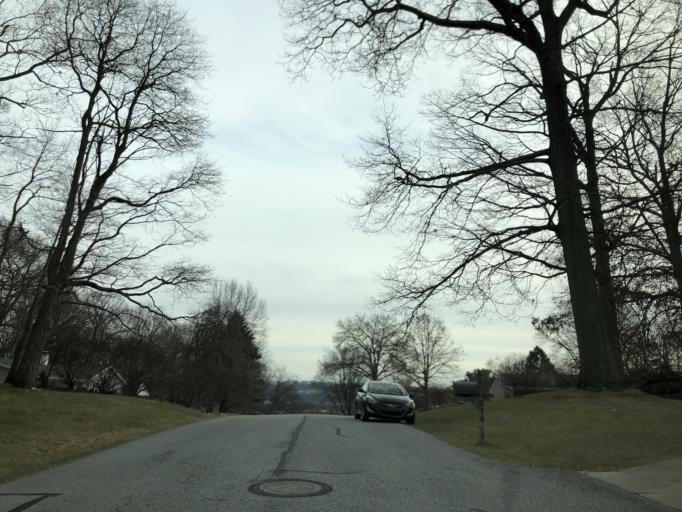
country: US
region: Pennsylvania
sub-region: Chester County
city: Exton
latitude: 40.0339
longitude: -75.6426
